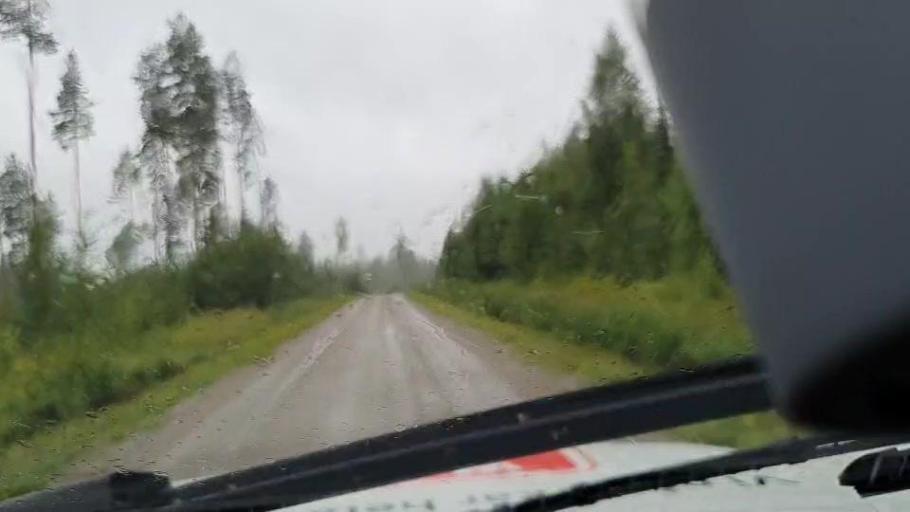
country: SE
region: Jaemtland
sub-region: OEstersunds Kommun
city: Brunflo
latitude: 62.8170
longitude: 15.0364
